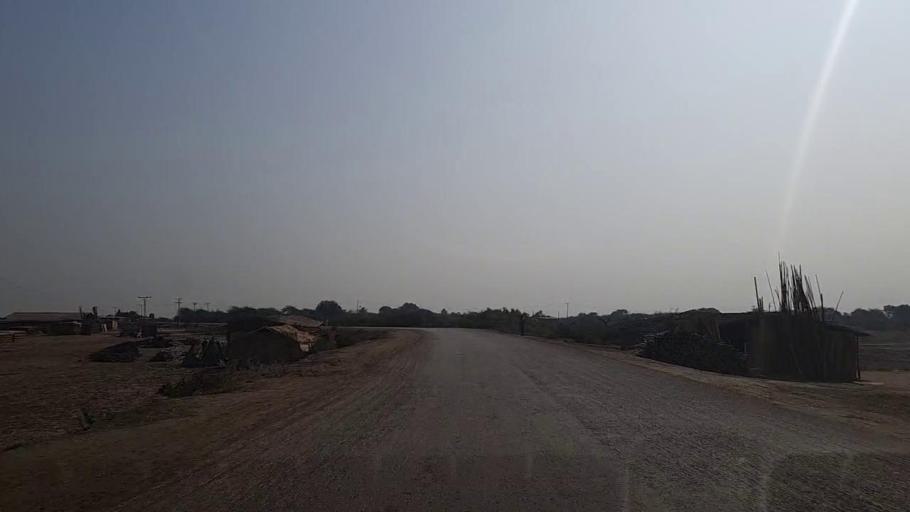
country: PK
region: Sindh
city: Keti Bandar
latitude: 24.2331
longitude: 67.6081
